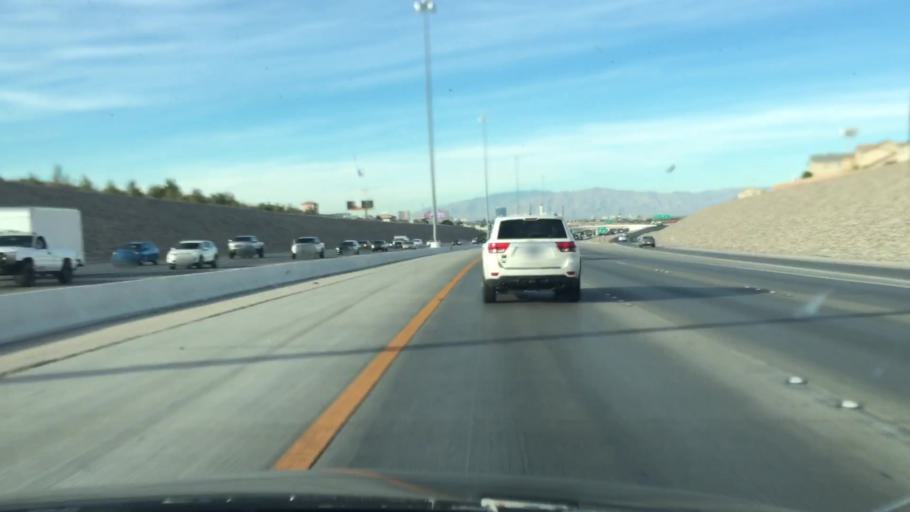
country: US
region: Nevada
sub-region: Clark County
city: Whitney
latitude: 36.0359
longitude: -115.1332
